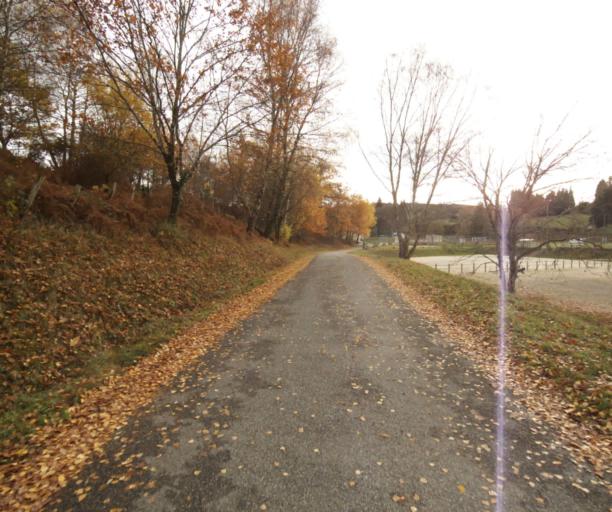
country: FR
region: Limousin
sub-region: Departement de la Correze
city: Sainte-Fortunade
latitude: 45.2071
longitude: 1.7742
